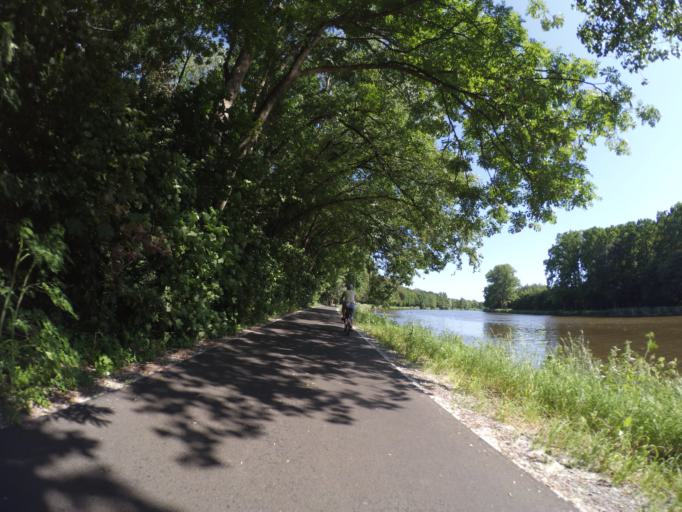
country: CZ
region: Central Bohemia
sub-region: Okres Nymburk
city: Nymburk
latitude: 50.1789
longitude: 15.0732
